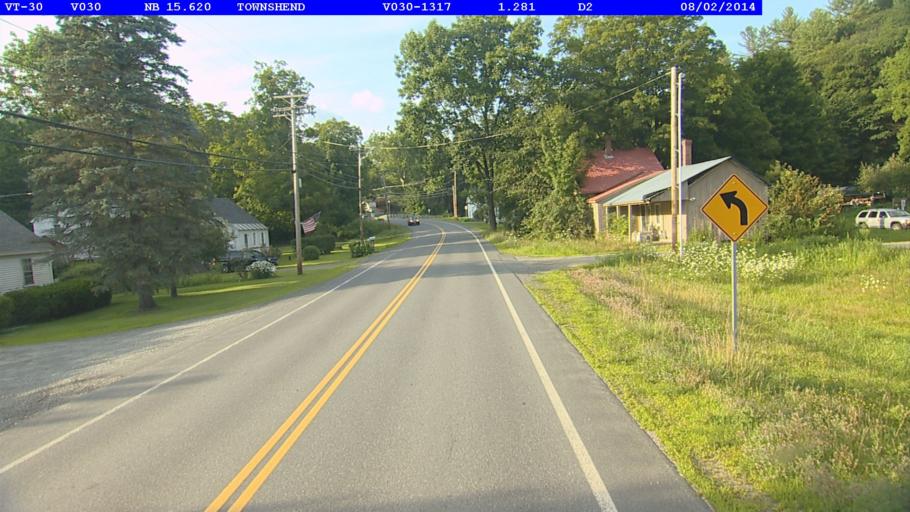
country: US
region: Vermont
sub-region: Windham County
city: Newfane
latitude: 43.0359
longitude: -72.6636
